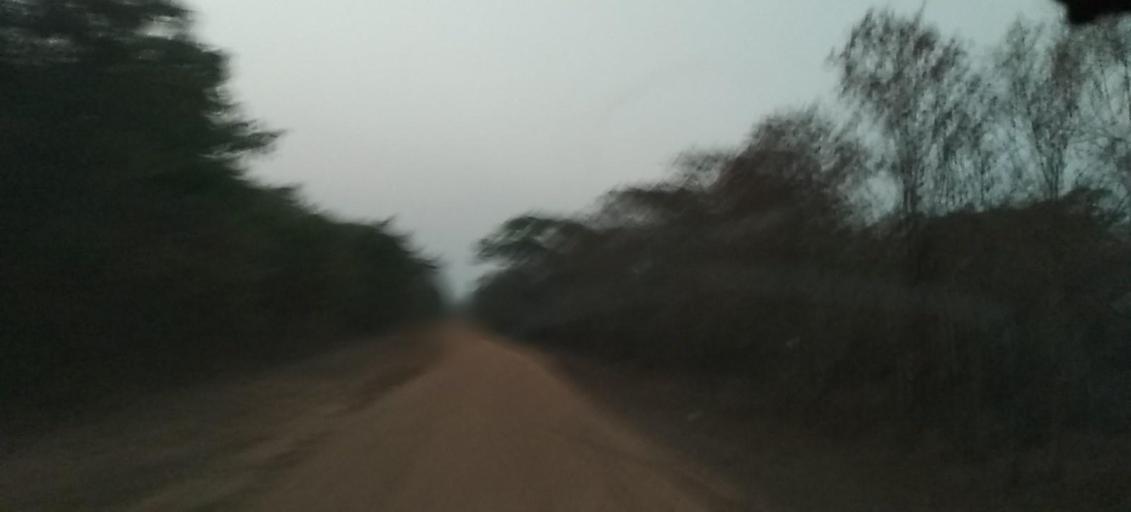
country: ZM
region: North-Western
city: Kasempa
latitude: -13.0745
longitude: 26.1526
